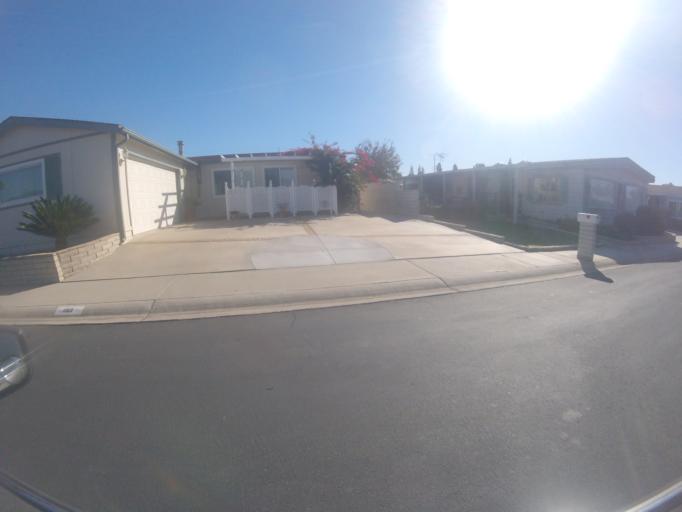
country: US
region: California
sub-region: San Bernardino County
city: Redlands
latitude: 34.0711
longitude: -117.1647
